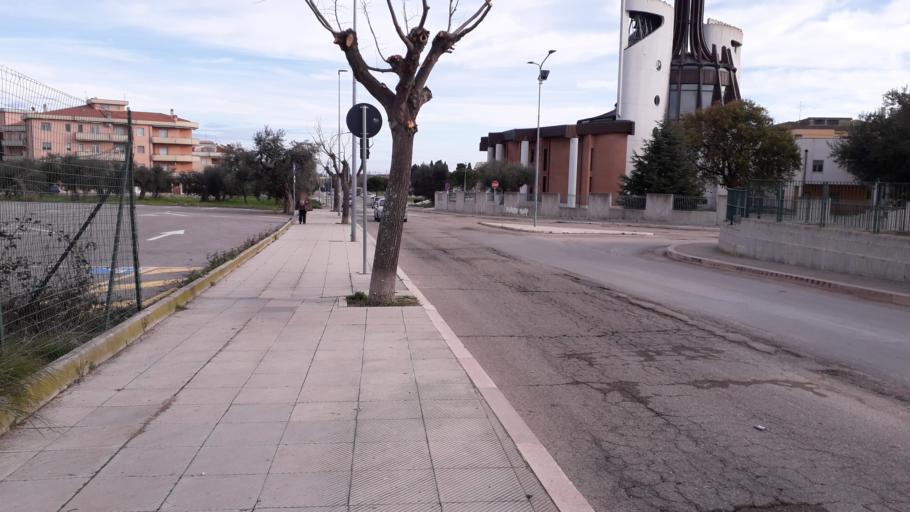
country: IT
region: Molise
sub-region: Provincia di Campobasso
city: Campomarino
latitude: 41.9510
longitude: 15.0330
